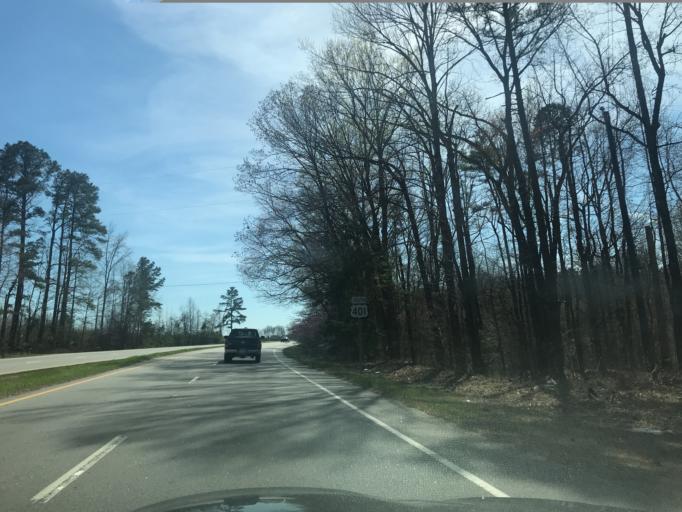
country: US
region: North Carolina
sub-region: Wake County
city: Garner
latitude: 35.6791
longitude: -78.6867
